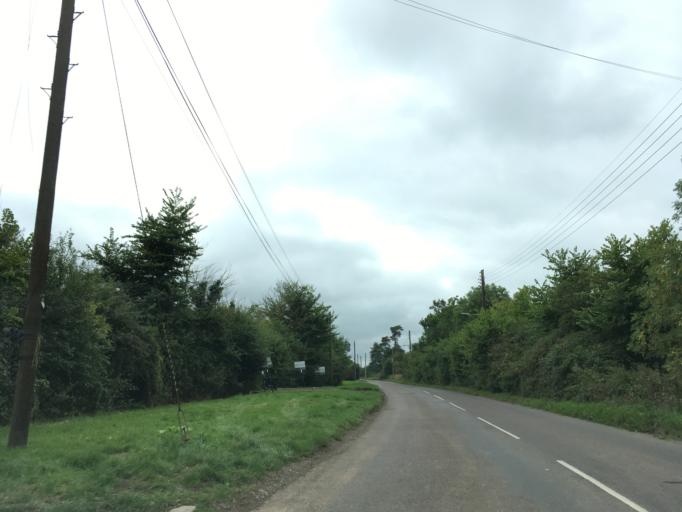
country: GB
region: England
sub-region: South Gloucestershire
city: Siston
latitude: 51.4653
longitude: -2.4588
